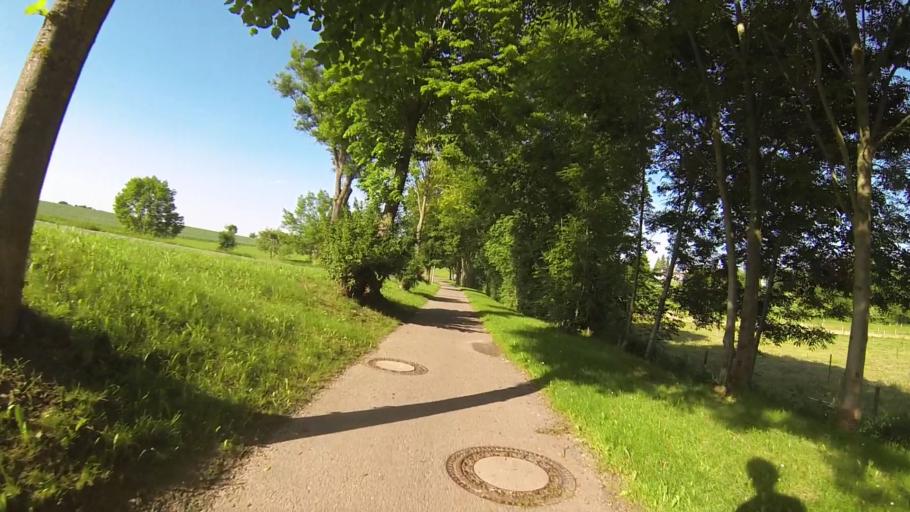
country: DE
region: Baden-Wuerttemberg
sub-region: Tuebingen Region
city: Maselheim
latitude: 48.1582
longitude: 9.8568
